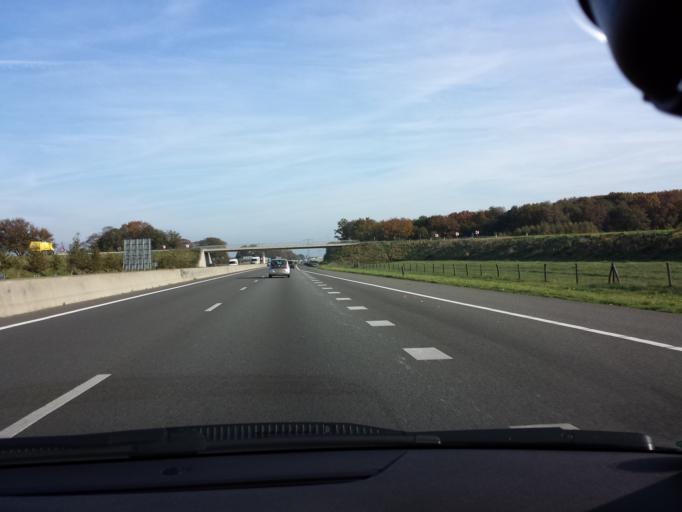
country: NL
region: Limburg
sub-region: Gemeente Maasgouw
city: Maasbracht
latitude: 51.1357
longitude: 5.9130
